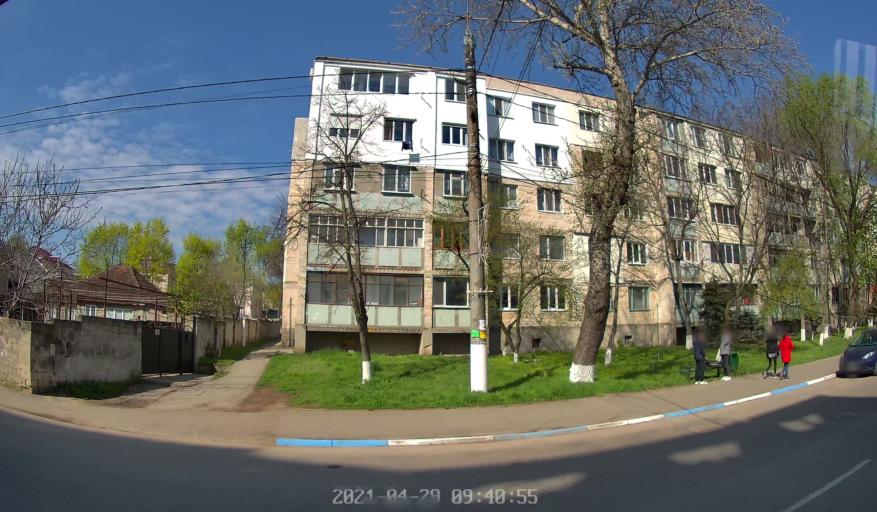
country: MD
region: Chisinau
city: Cricova
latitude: 47.1384
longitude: 28.8664
